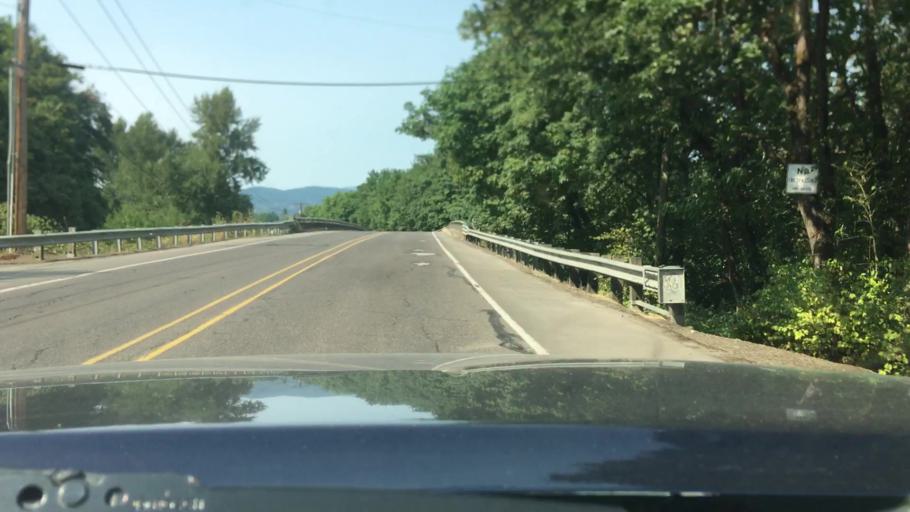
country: US
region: Oregon
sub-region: Lane County
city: Springfield
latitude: 44.0293
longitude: -123.0268
